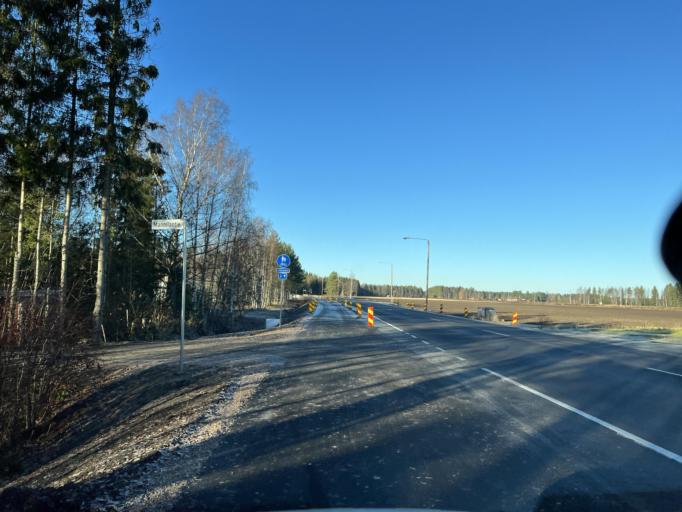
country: FI
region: Northern Ostrobothnia
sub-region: Nivala-Haapajaervi
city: Nivala
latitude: 63.9482
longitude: 24.9243
